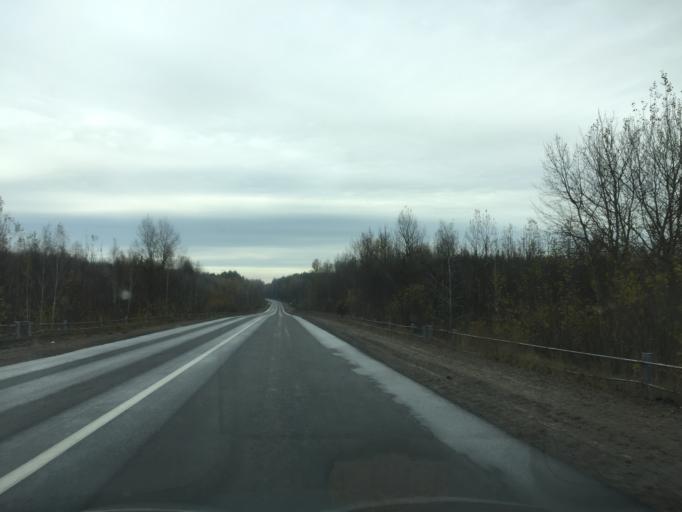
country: BY
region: Gomel
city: Gomel
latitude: 52.4195
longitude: 30.8285
